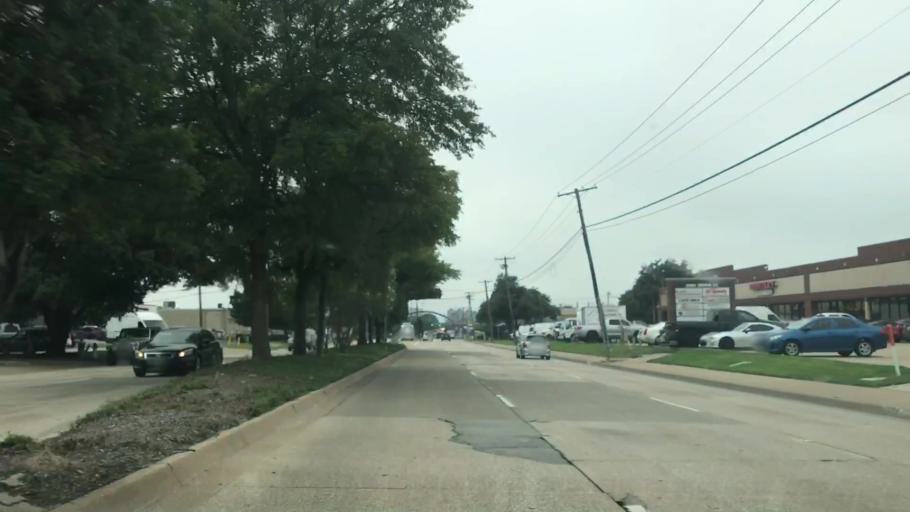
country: US
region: Texas
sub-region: Dallas County
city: Addison
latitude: 32.9616
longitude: -96.8385
